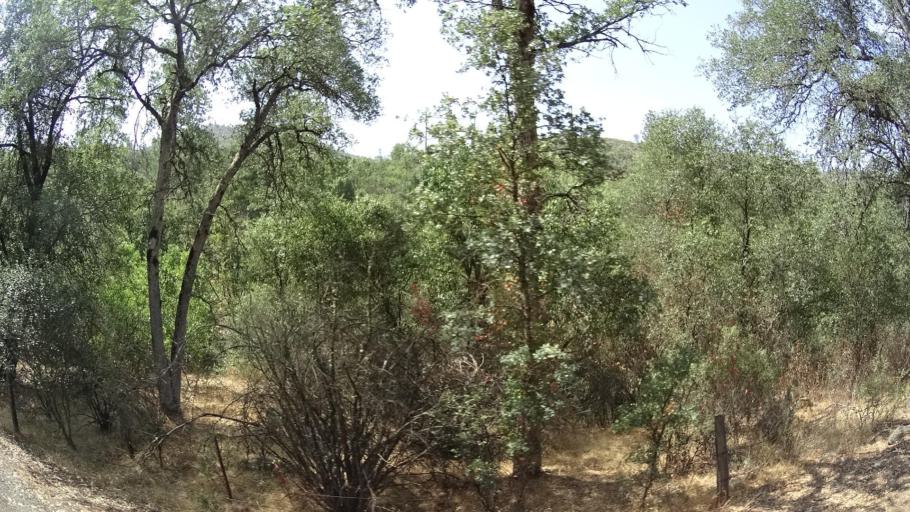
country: US
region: California
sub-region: Tuolumne County
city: Tuolumne City
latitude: 37.7071
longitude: -120.1629
